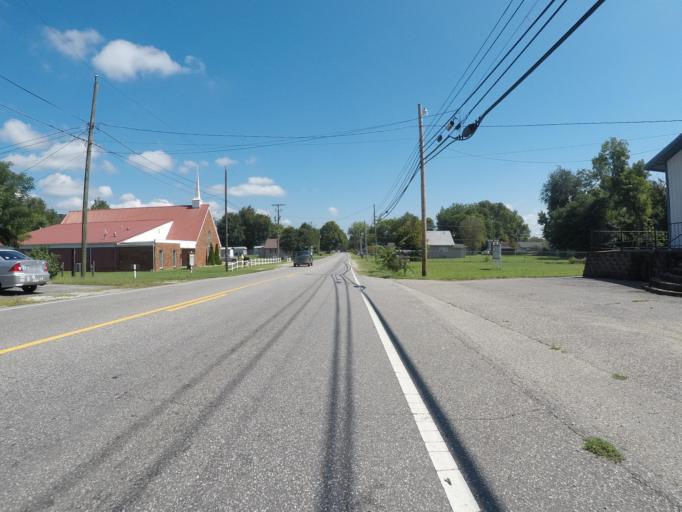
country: US
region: Ohio
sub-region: Lawrence County
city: Burlington
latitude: 38.4075
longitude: -82.5290
